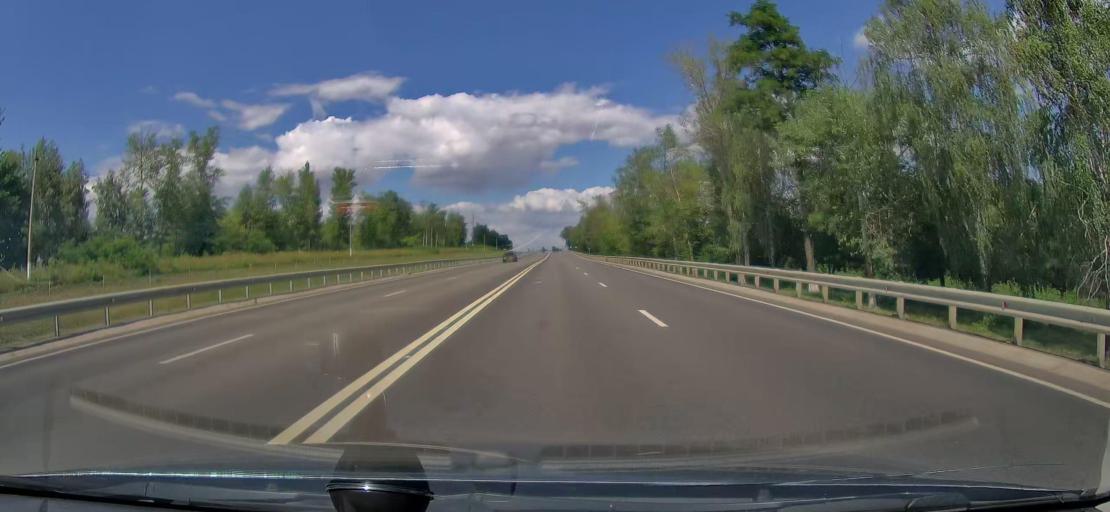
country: RU
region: Kursk
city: Zolotukhino
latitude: 51.9555
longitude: 36.3050
